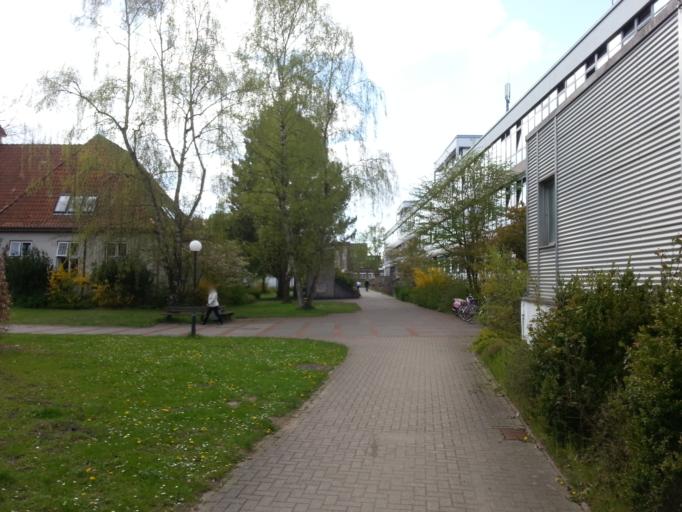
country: DE
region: Schleswig-Holstein
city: Luebeck
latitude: 53.8381
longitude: 10.7064
